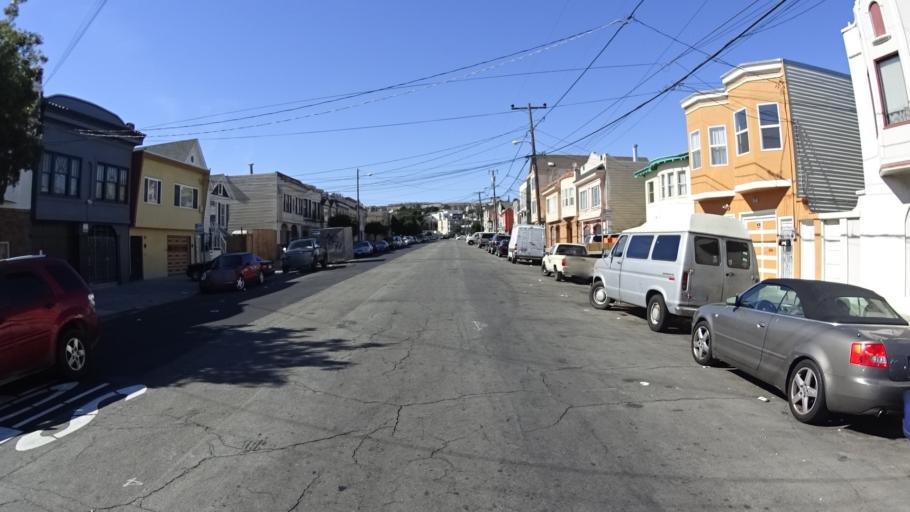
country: US
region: California
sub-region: San Mateo County
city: Brisbane
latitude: 37.7300
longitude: -122.3889
